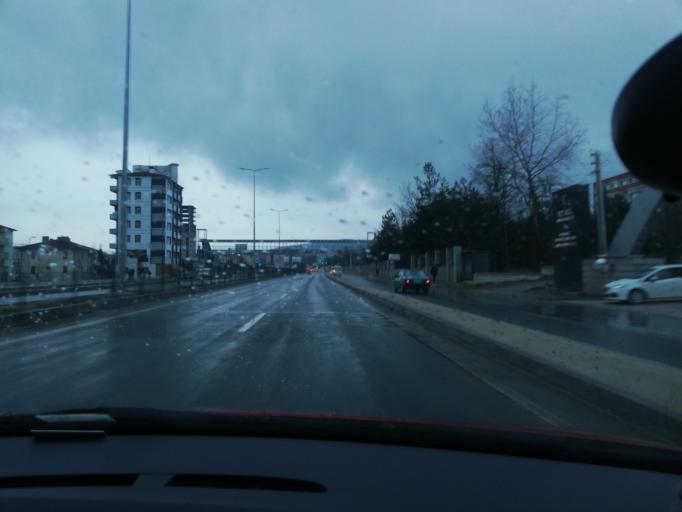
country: TR
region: Kastamonu
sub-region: Cide
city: Kastamonu
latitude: 41.4133
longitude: 33.7938
